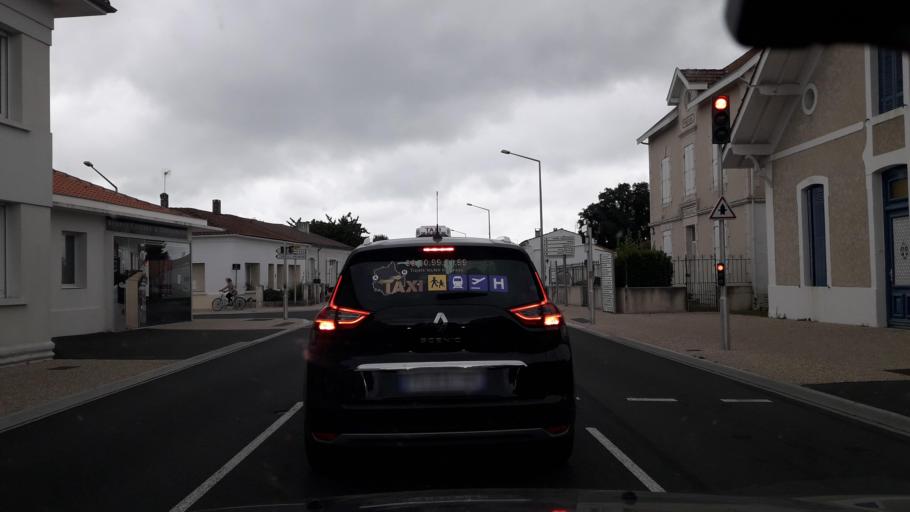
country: FR
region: Poitou-Charentes
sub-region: Departement de la Charente-Maritime
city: Arvert
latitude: 45.7425
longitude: -1.1236
